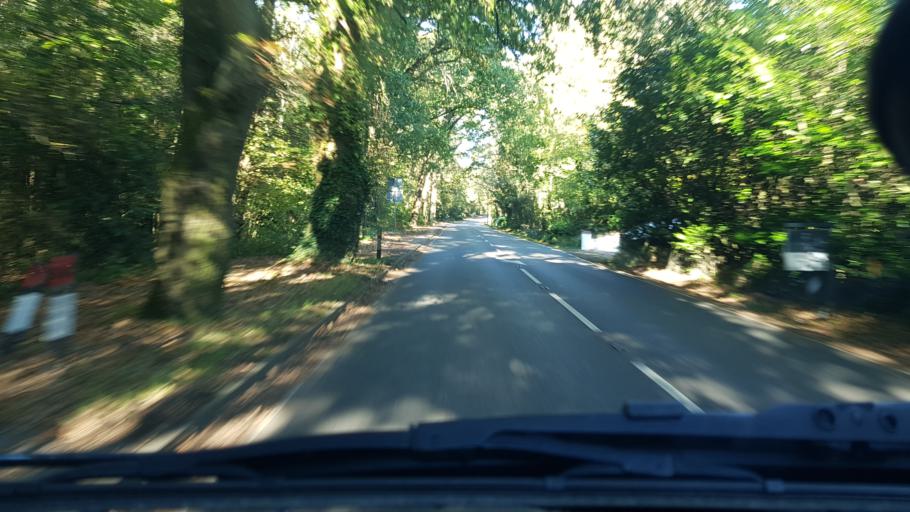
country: GB
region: England
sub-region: Surrey
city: Pirbright
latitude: 51.2846
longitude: -0.6437
